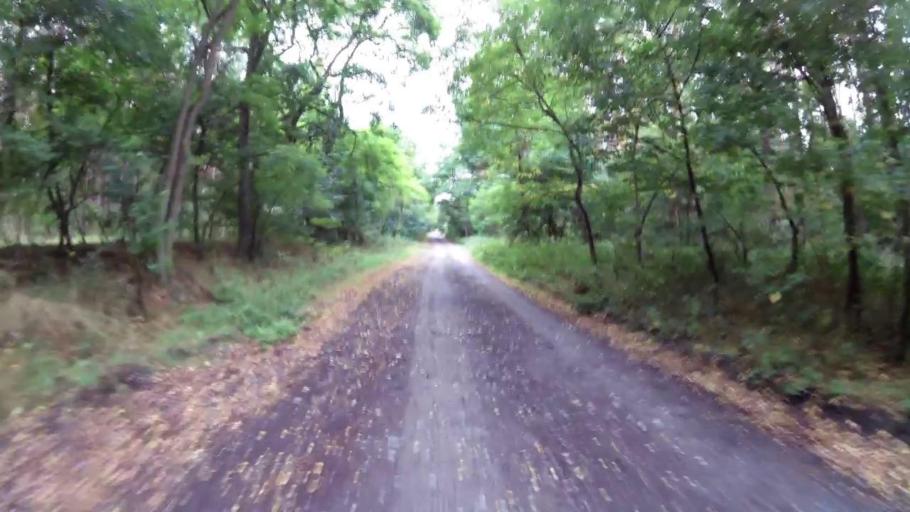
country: PL
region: West Pomeranian Voivodeship
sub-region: Powiat mysliborski
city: Debno
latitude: 52.8537
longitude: 14.7214
